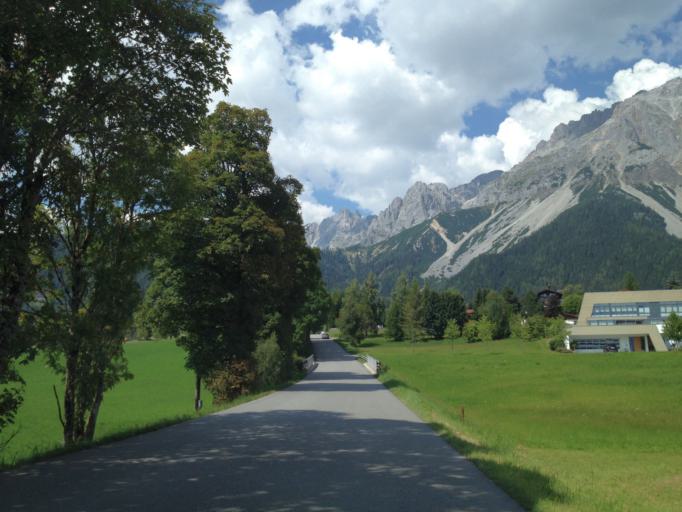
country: AT
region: Styria
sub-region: Politischer Bezirk Liezen
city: Schladming
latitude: 47.4219
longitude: 13.6360
